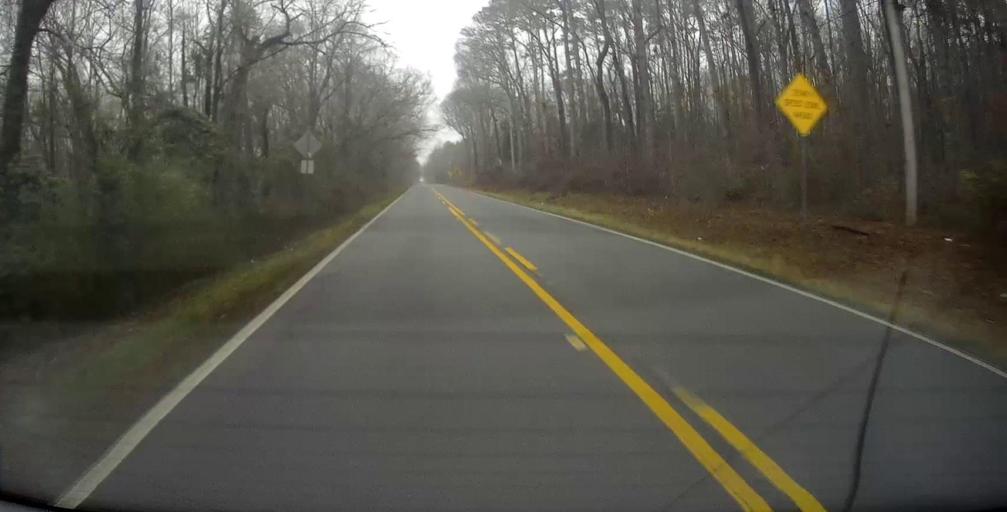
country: US
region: Georgia
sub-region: Spalding County
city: East Griffin
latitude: 33.2265
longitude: -84.2420
